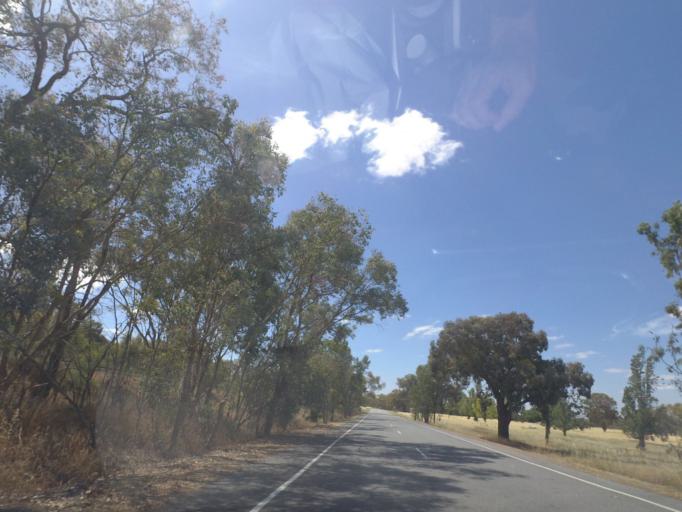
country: AU
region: Victoria
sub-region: Wangaratta
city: Wangaratta
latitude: -36.4533
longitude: 146.2375
